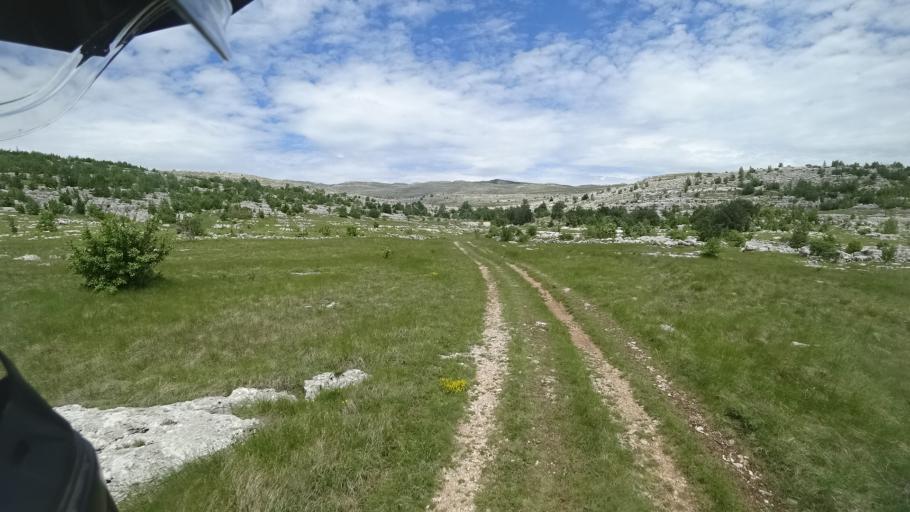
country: HR
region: Splitsko-Dalmatinska
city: Hrvace
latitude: 43.8927
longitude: 16.5853
